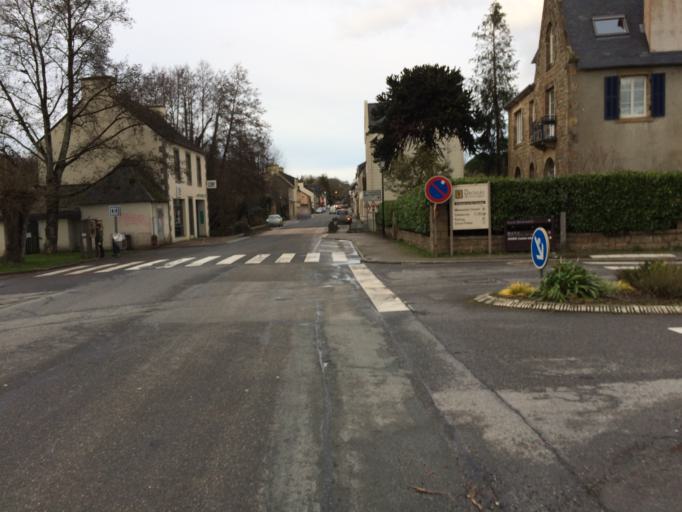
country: FR
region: Brittany
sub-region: Departement du Finistere
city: Daoulas
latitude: 48.3592
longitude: -4.2598
